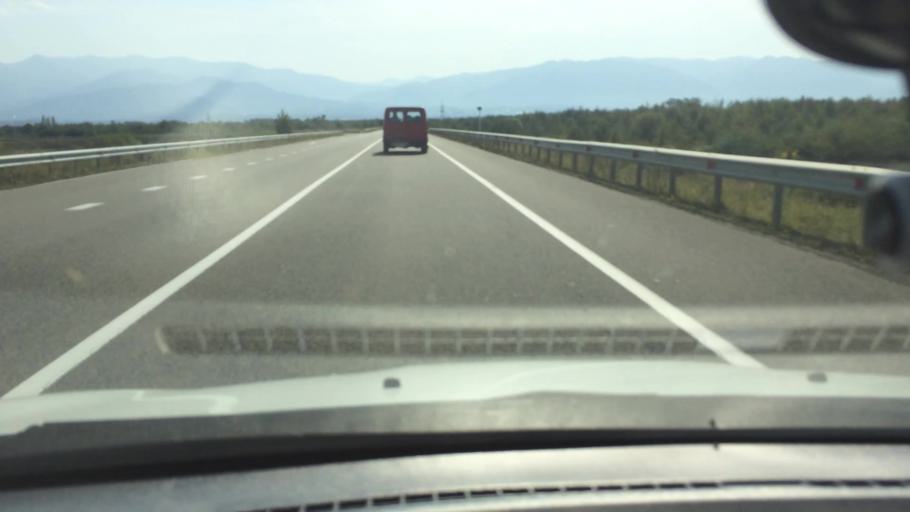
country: GE
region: Ajaria
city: Ochkhamuri
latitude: 41.8980
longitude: 41.7979
